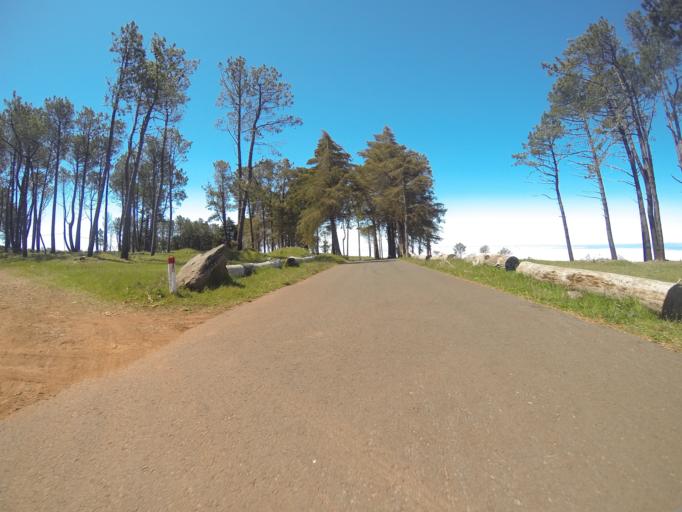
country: PT
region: Madeira
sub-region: Funchal
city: Nossa Senhora do Monte
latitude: 32.7109
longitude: -16.9119
